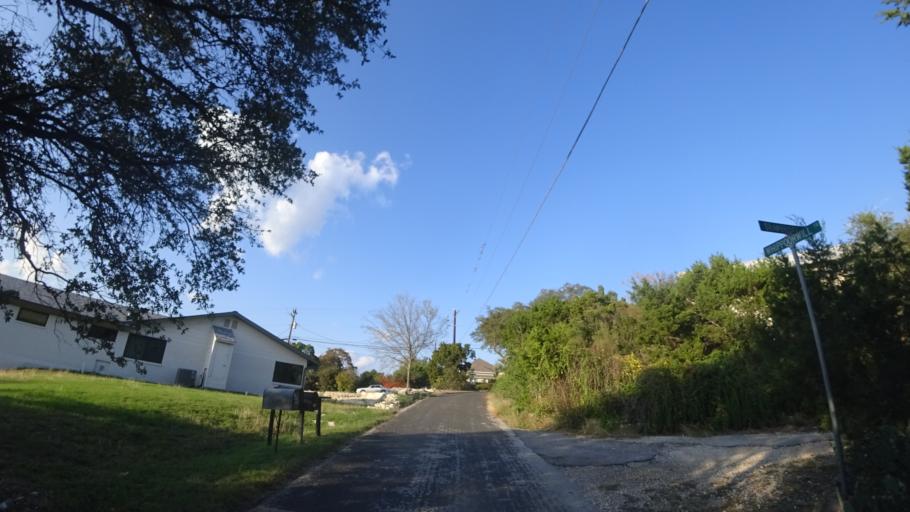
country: US
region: Texas
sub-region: Travis County
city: Lost Creek
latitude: 30.2958
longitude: -97.8420
